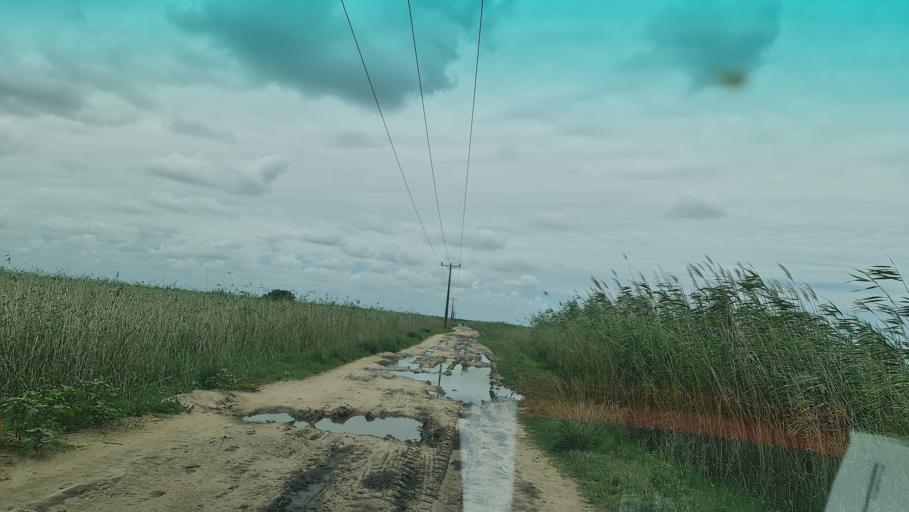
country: MZ
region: Maputo City
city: Maputo
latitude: -25.7204
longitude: 32.6997
